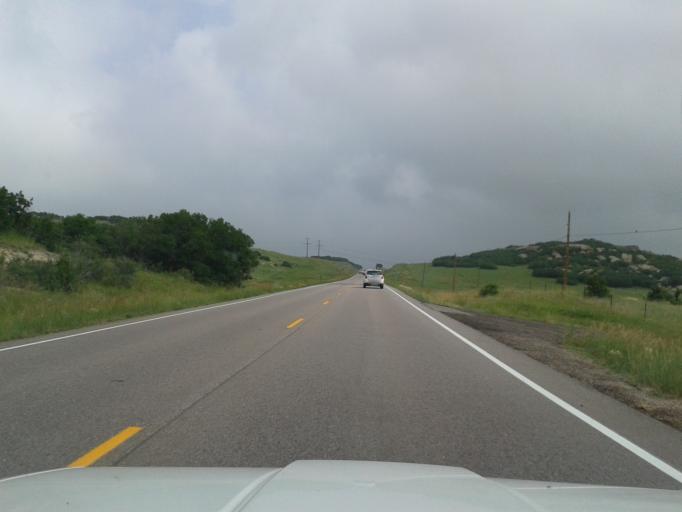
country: US
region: Colorado
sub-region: Douglas County
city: Castle Rock
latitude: 39.2790
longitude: -104.7368
